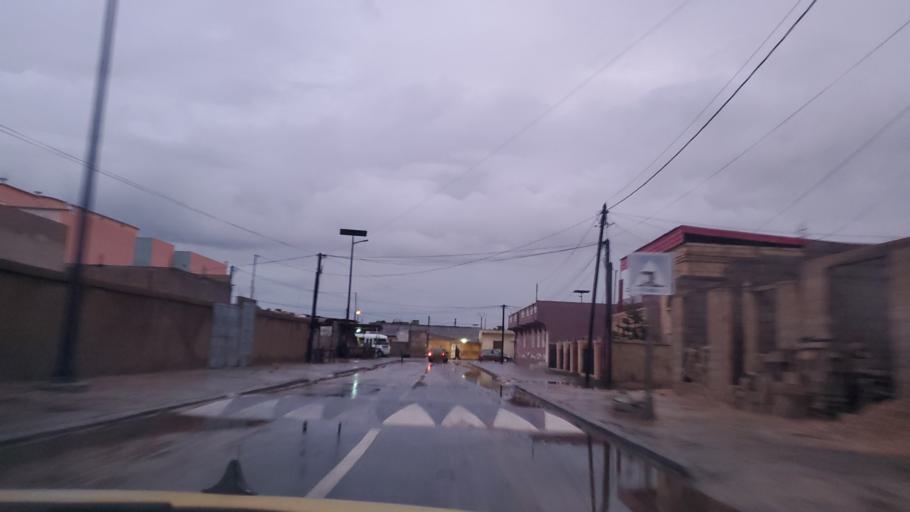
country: SN
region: Saint-Louis
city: Saint-Louis
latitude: 16.0104
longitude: -16.4935
